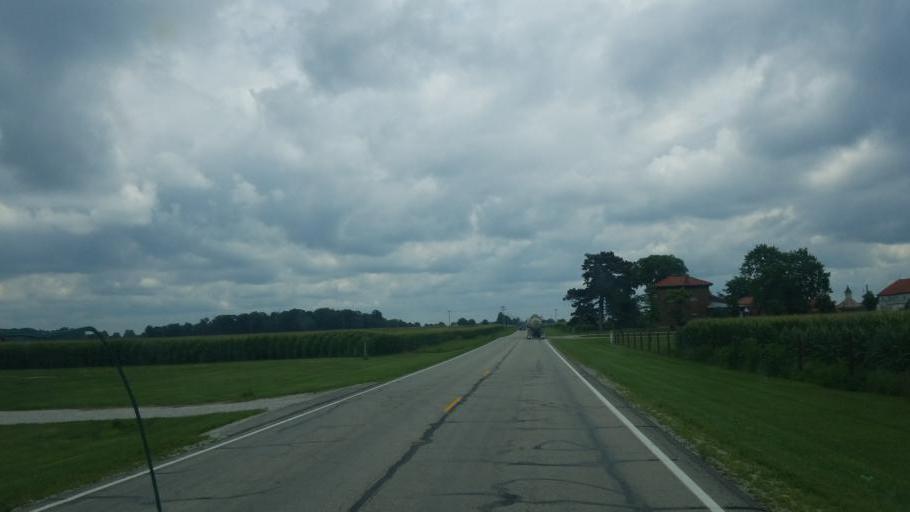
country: US
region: Indiana
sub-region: Wells County
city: Bluffton
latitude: 40.6546
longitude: -85.2069
